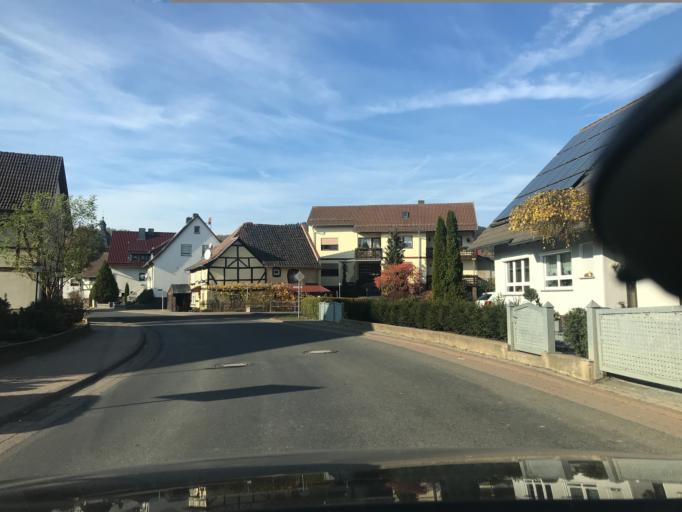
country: DE
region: Hesse
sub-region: Regierungsbezirk Kassel
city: Grossalmerode
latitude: 51.2139
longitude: 9.7982
